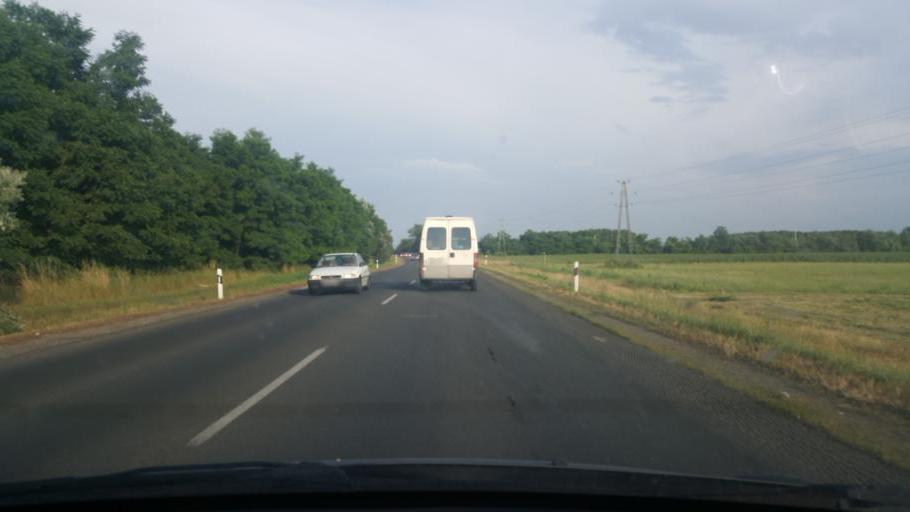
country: HU
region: Pest
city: Peteri
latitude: 47.3624
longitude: 19.3871
